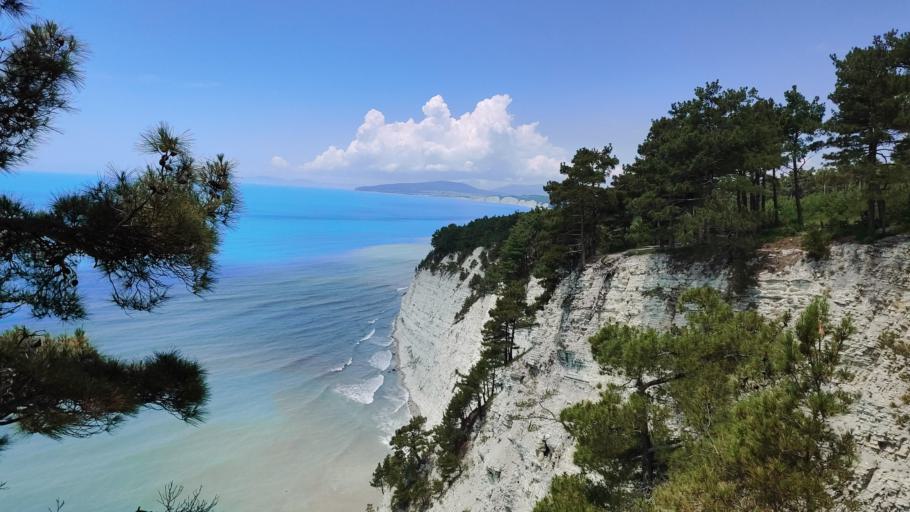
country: RU
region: Krasnodarskiy
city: Divnomorskoye
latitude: 44.4759
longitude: 38.1440
